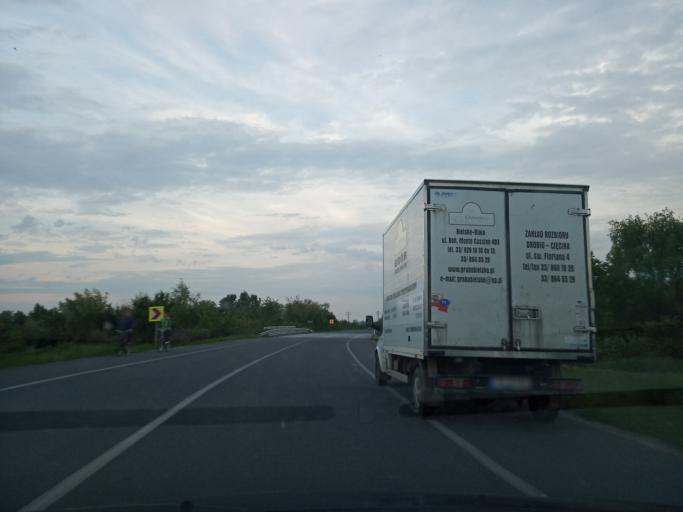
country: RO
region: Timis
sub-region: Oras Deta
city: Deta
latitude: 45.3918
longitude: 21.2320
